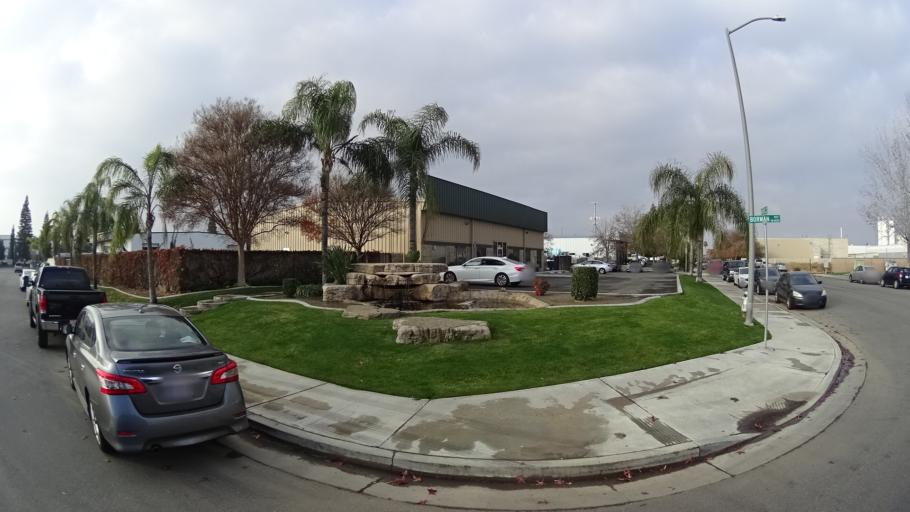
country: US
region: California
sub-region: Kern County
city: Greenacres
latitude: 35.3145
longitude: -119.0762
